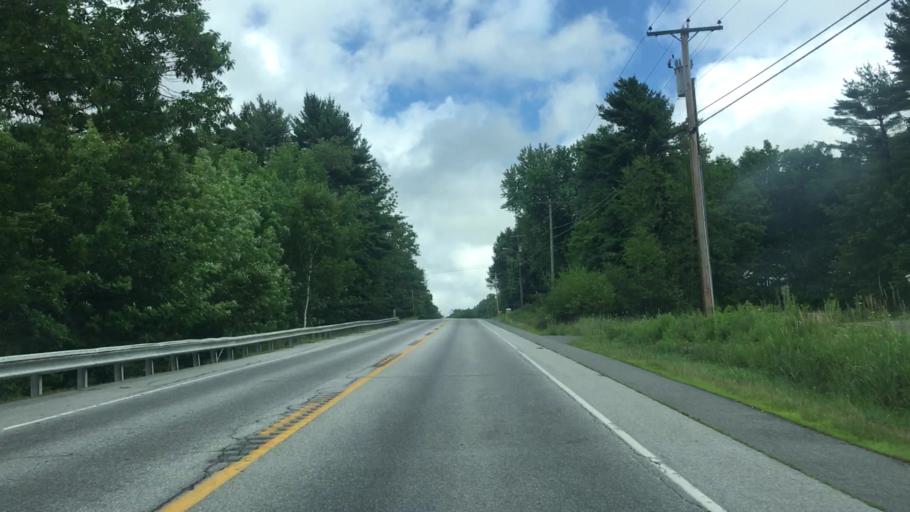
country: US
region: Maine
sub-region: Kennebec County
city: Farmingdale
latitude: 44.2592
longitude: -69.7648
